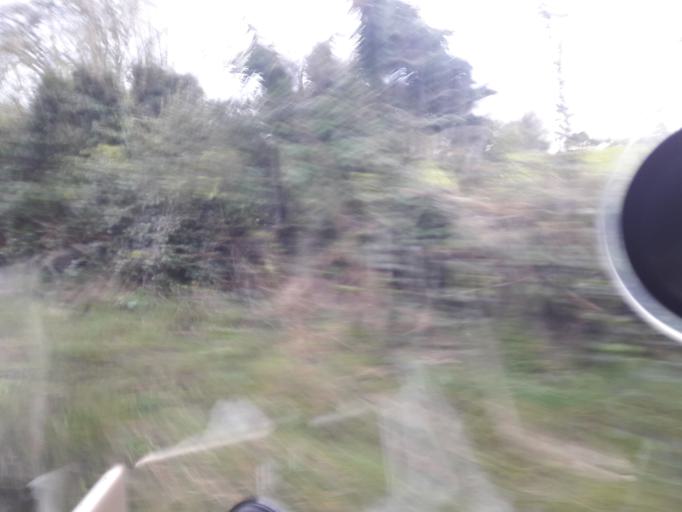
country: IE
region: Leinster
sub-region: An Iarmhi
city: An Muileann gCearr
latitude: 53.5128
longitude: -7.3205
